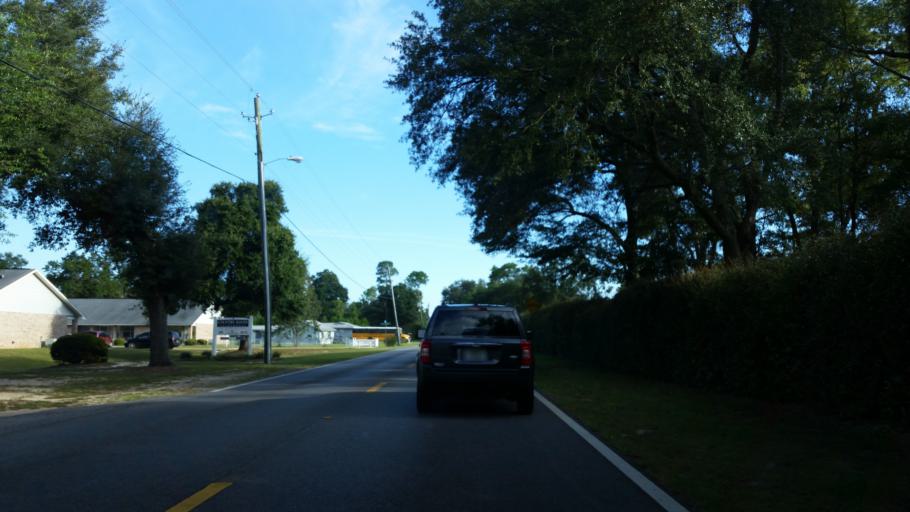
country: US
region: Florida
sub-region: Santa Rosa County
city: Milton
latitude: 30.6254
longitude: -87.0643
